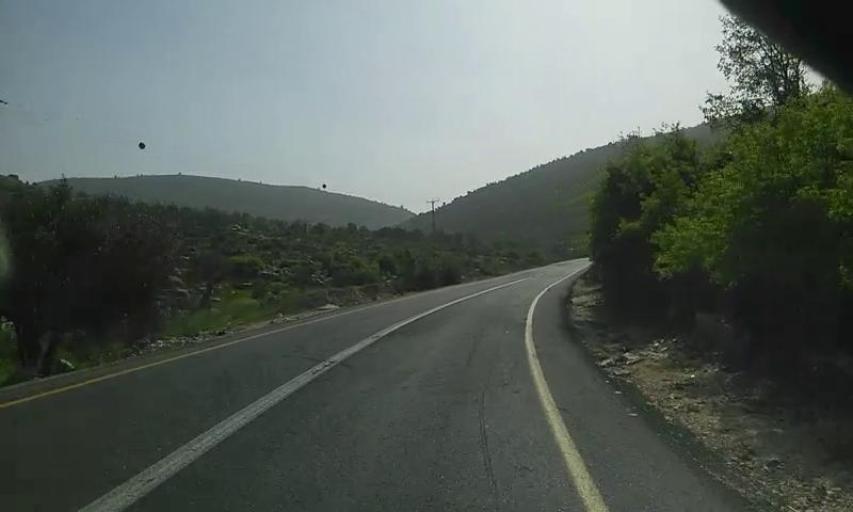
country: PS
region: West Bank
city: `Atarah
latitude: 31.9996
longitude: 35.2320
